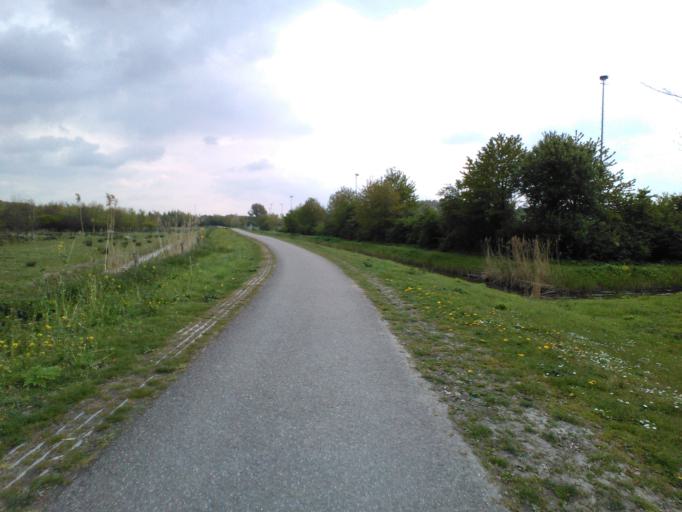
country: NL
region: South Holland
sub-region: Gemeente Vlaardingen
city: Vlaardingen
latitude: 51.9224
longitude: 4.3198
